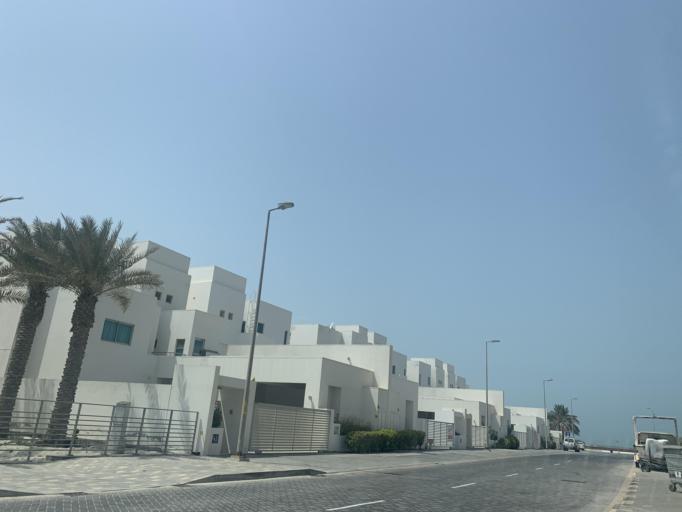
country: BH
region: Muharraq
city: Al Hadd
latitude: 26.2747
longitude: 50.6716
